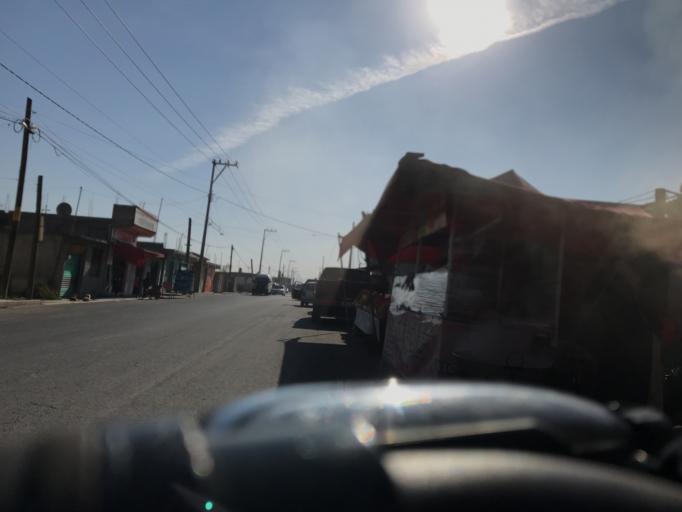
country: MX
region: Mexico
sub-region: Tonanitla
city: Colonia la Asuncion
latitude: 19.6922
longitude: -99.0627
